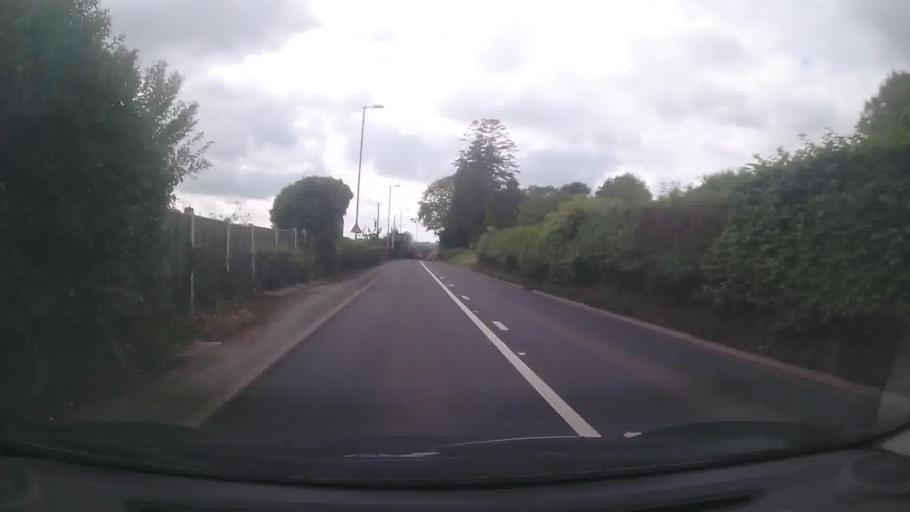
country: GB
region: England
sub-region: Shropshire
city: Pant
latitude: 52.7889
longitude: -3.0810
